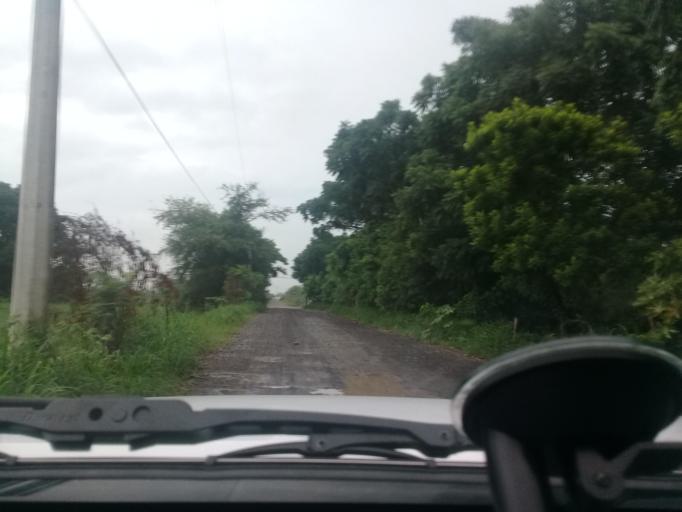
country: MX
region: Veracruz
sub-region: La Antigua
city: Nicolas Blanco (San Pancho)
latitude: 19.3506
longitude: -96.3436
